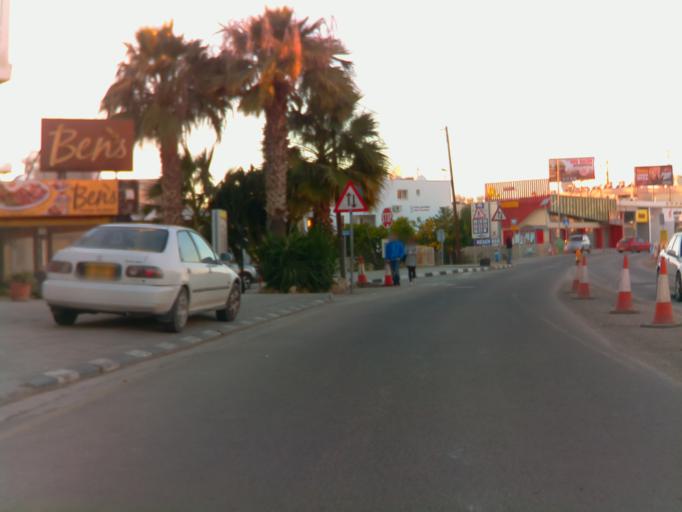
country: CY
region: Pafos
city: Paphos
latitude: 34.7648
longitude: 32.4114
